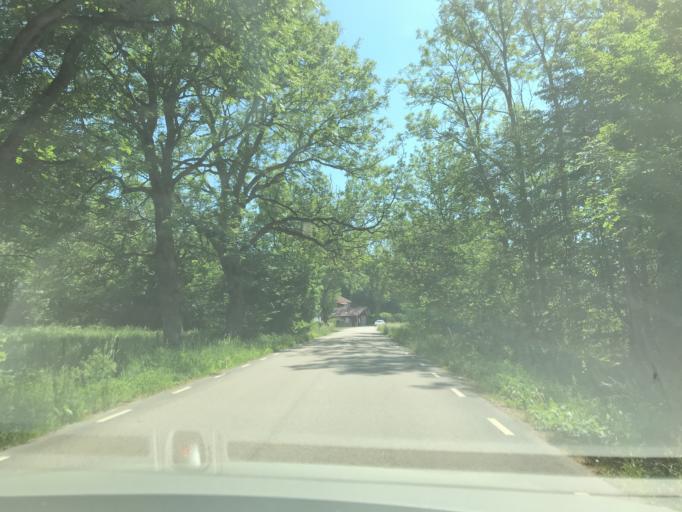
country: SE
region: Vaestra Goetaland
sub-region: Gotene Kommun
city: Kallby
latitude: 58.5556
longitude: 13.3465
